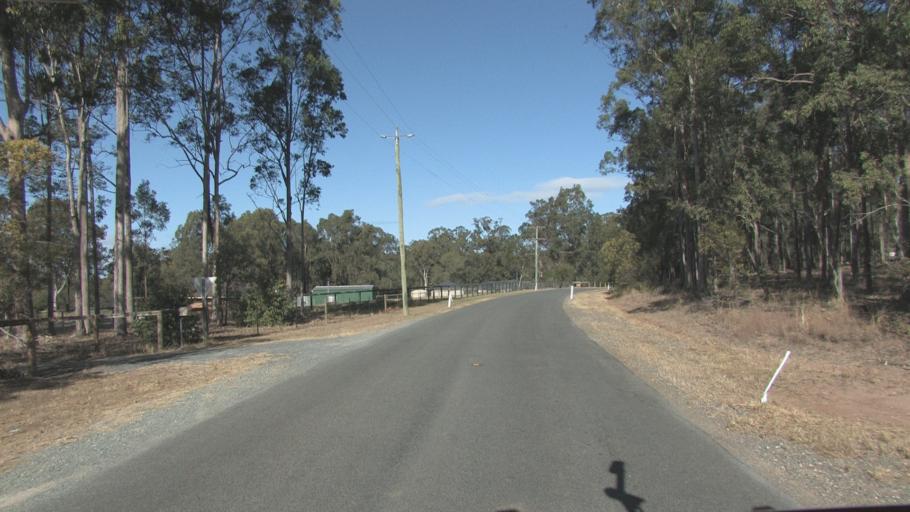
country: AU
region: Queensland
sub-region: Logan
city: Cedar Vale
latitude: -27.8545
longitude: 152.9932
